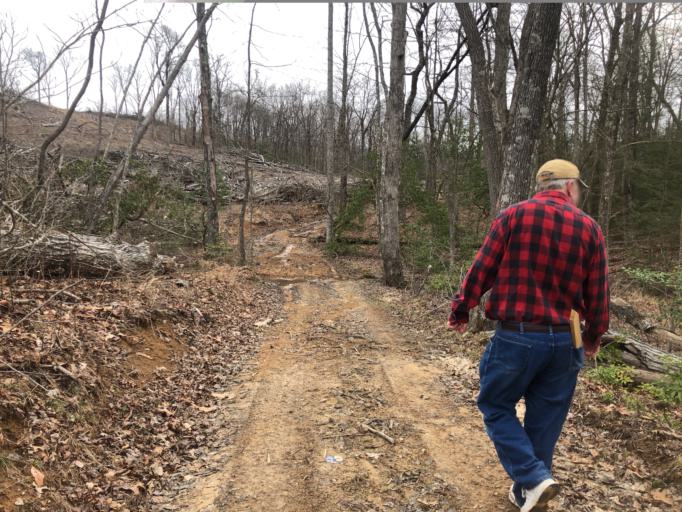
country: US
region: Tennessee
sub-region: Cumberland County
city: Fairfield Glade
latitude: 35.9700
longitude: -84.7637
